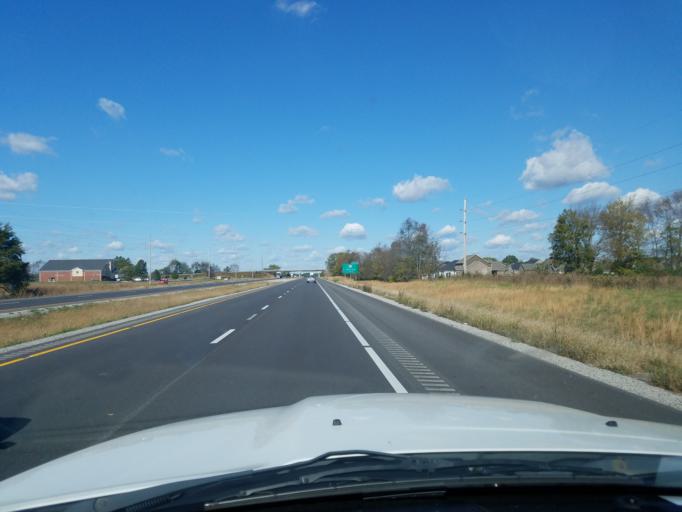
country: US
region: Kentucky
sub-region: Warren County
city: Plano
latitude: 36.9230
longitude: -86.4495
